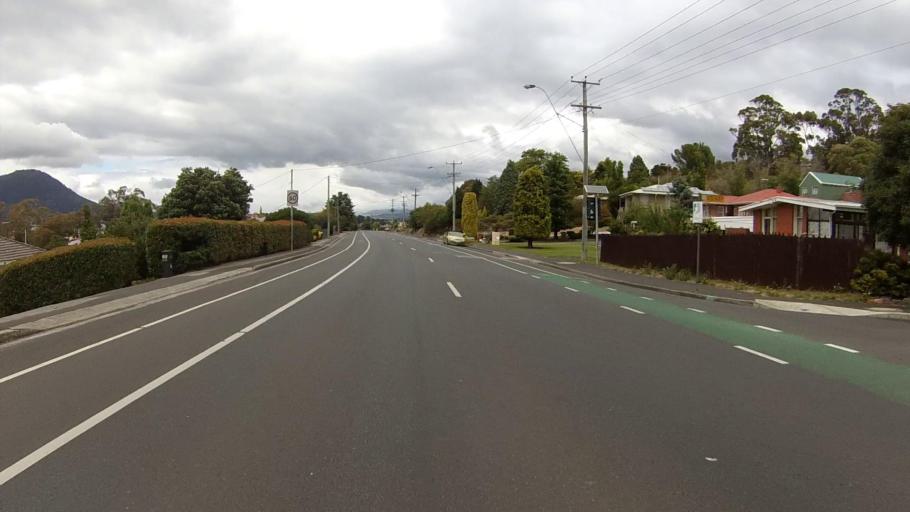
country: AU
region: Tasmania
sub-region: Glenorchy
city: Claremont
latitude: -42.7763
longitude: 147.2506
